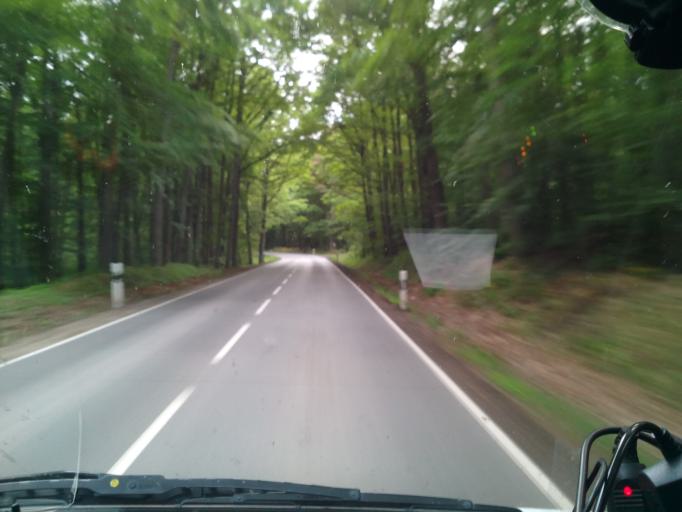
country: DE
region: Thuringia
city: Hellingen
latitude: 50.2702
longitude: 10.7044
